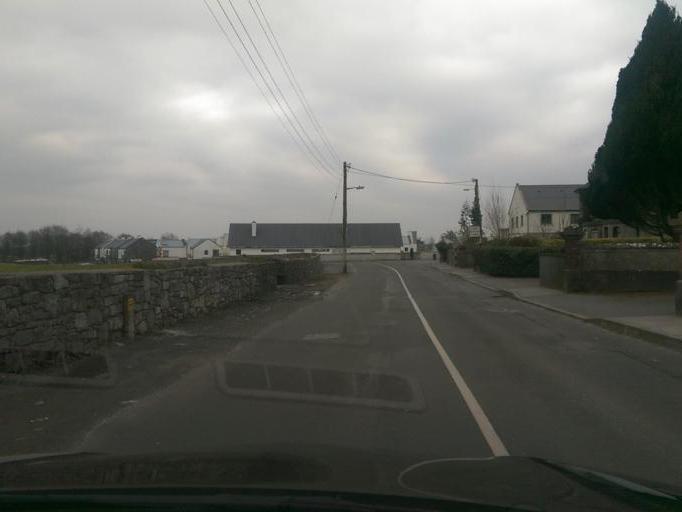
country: IE
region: Connaught
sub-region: County Galway
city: Athenry
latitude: 53.2953
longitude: -8.7514
